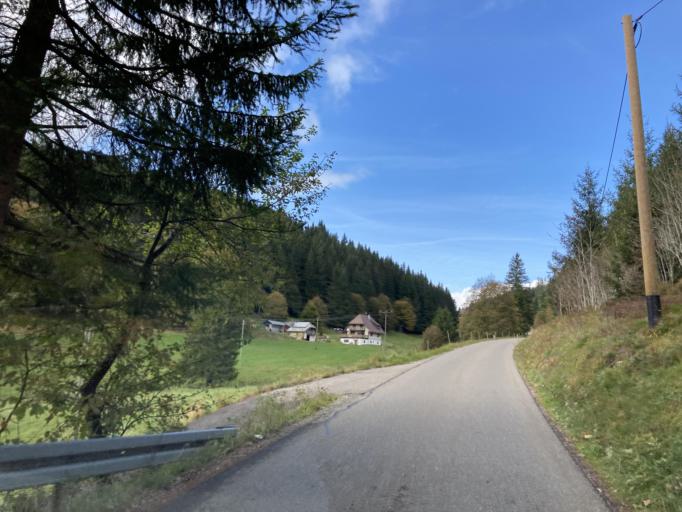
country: DE
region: Baden-Wuerttemberg
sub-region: Freiburg Region
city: Vohrenbach
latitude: 48.0594
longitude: 8.2859
